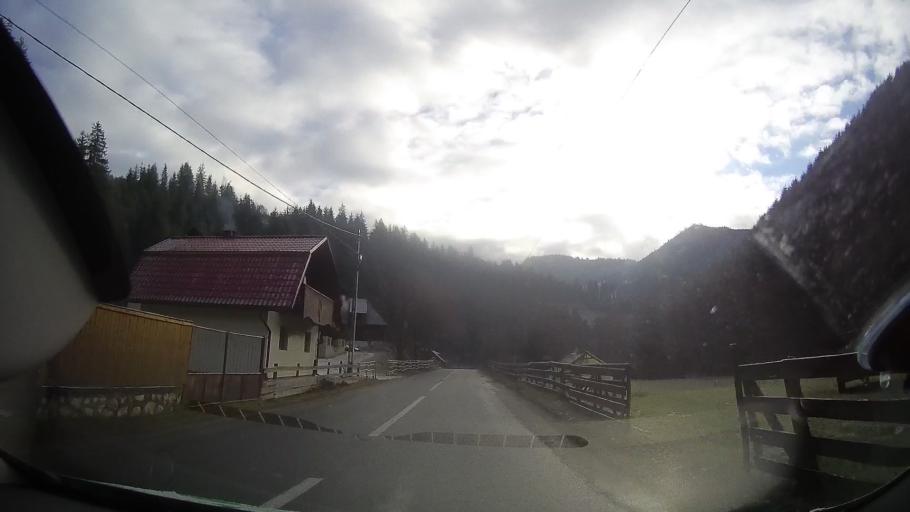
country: RO
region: Alba
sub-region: Comuna Albac
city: Albac
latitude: 46.4608
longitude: 22.9734
